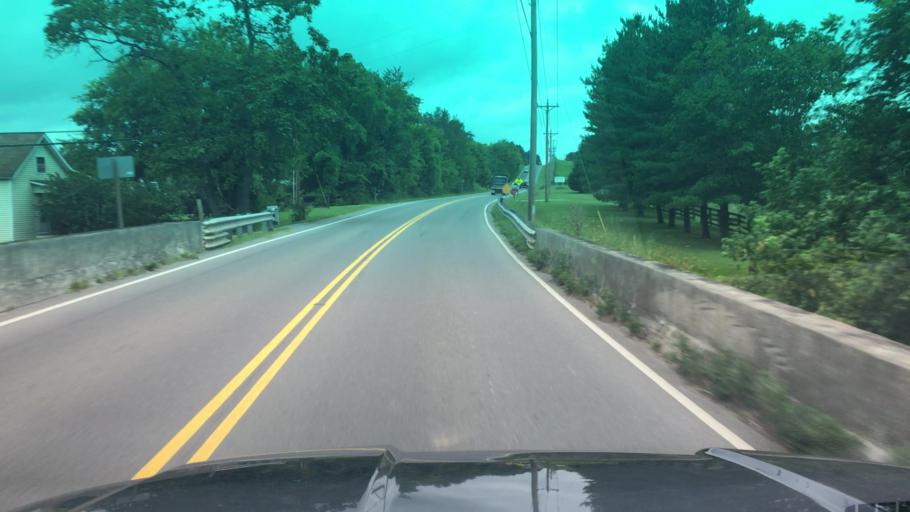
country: US
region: Tennessee
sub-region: Williamson County
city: Thompson's Station
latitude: 35.8101
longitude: -86.8522
